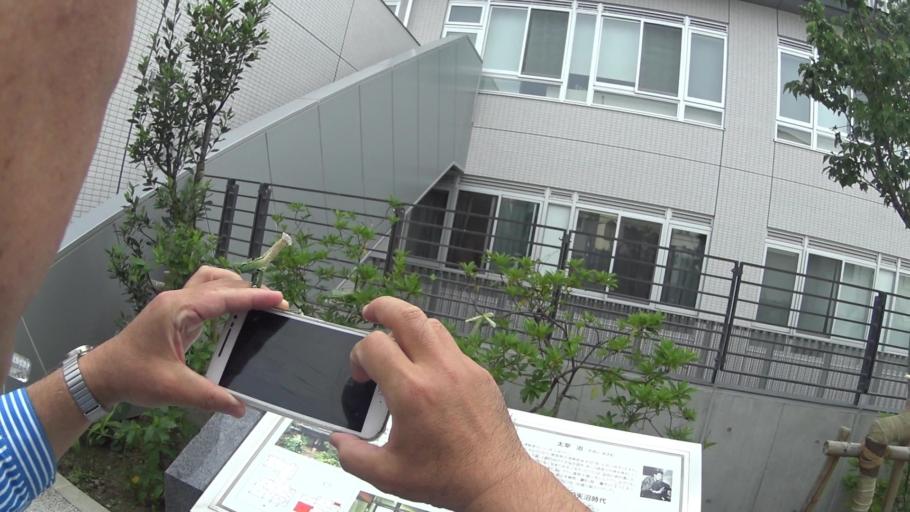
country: JP
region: Tokyo
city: Musashino
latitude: 35.7103
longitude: 139.6211
